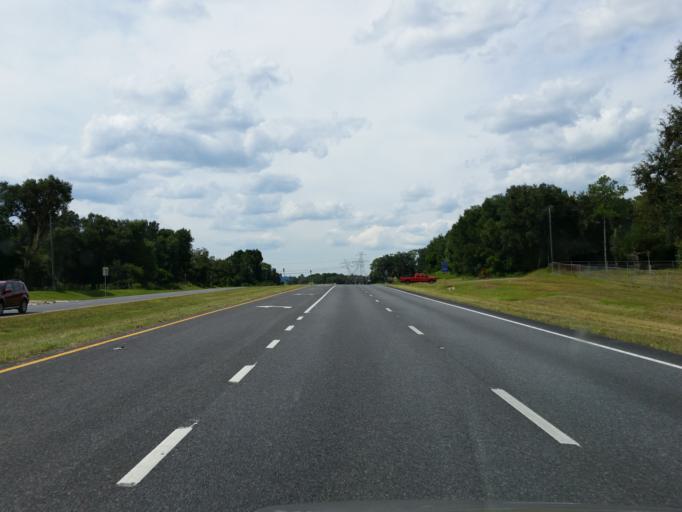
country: US
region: Florida
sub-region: Sumter County
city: Wildwood
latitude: 28.8648
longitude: -82.0780
